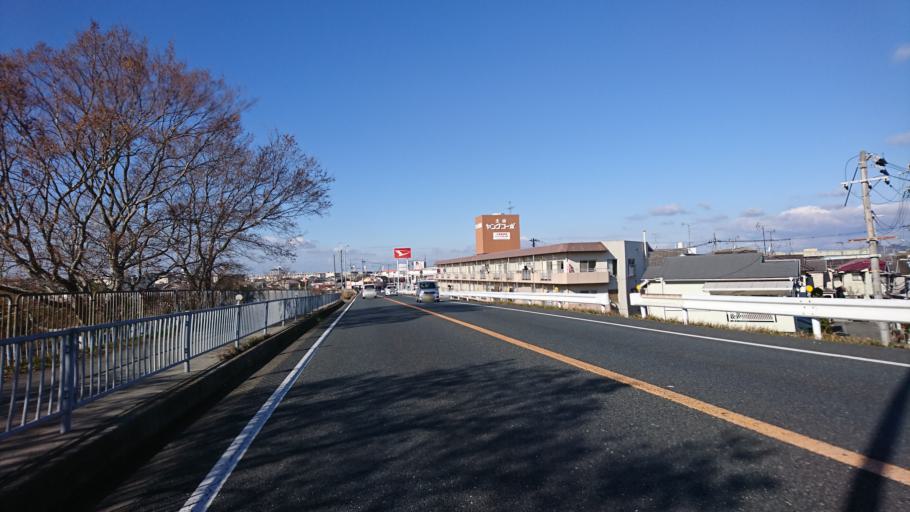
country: JP
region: Hyogo
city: Kakogawacho-honmachi
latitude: 34.7282
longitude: 134.8841
